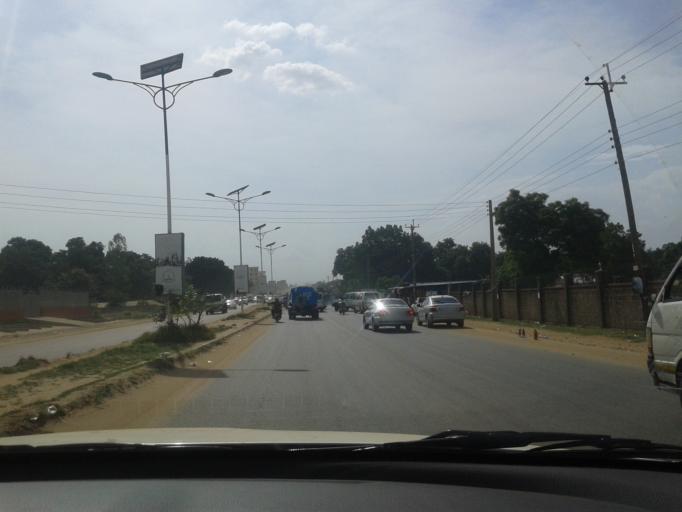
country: SS
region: Central Equatoria
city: Juba
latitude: 4.8565
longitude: 31.5773
